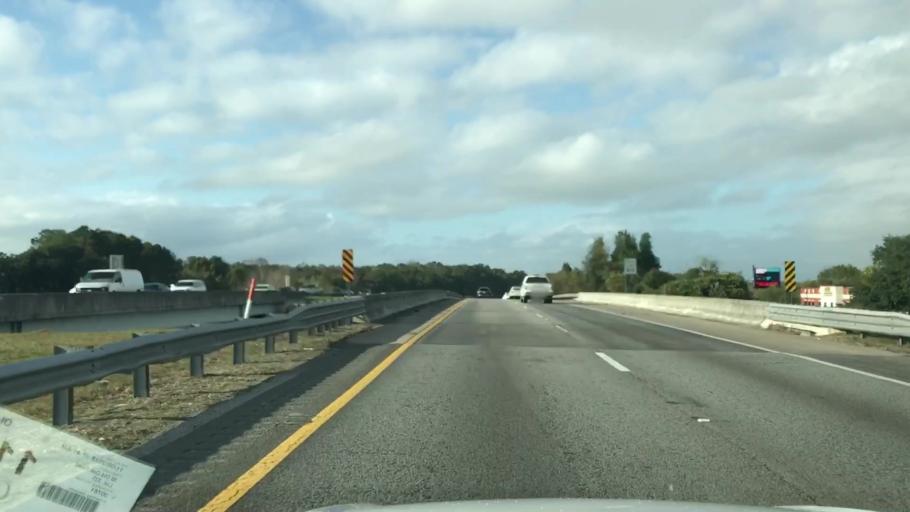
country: US
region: South Carolina
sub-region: Charleston County
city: North Charleston
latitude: 32.8625
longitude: -80.0256
